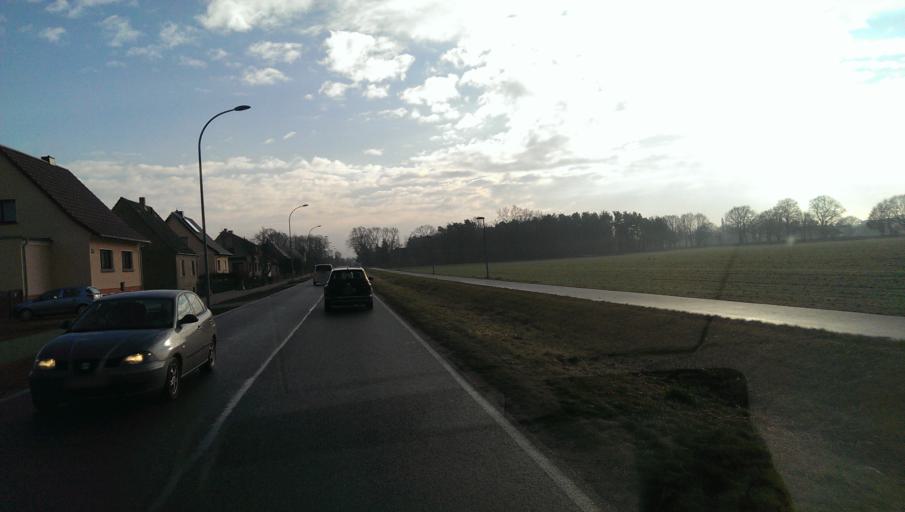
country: DE
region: Brandenburg
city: Herzberg
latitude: 51.7054
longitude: 13.2404
